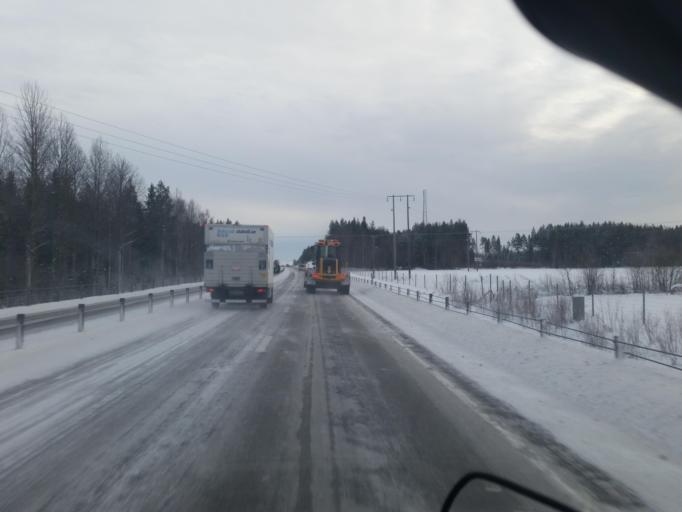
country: SE
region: Norrbotten
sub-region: Pitea Kommun
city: Pitea
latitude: 65.2543
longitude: 21.4736
